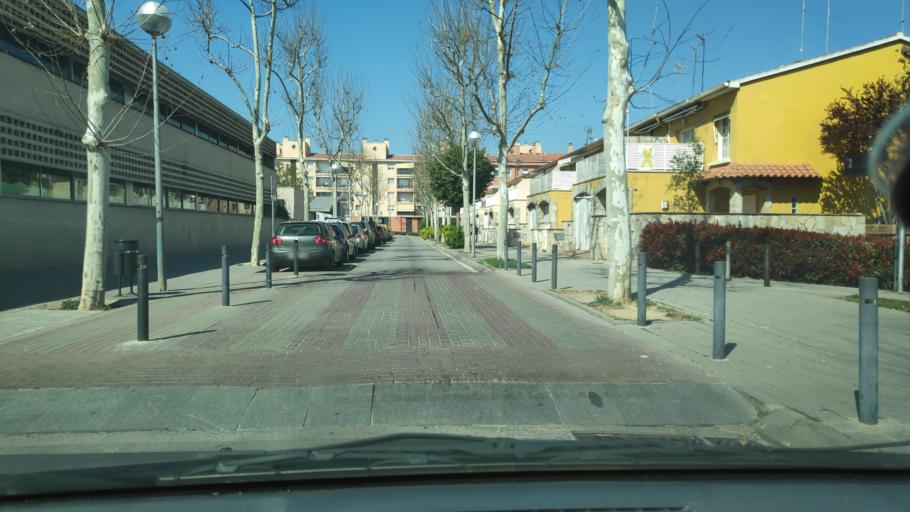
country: ES
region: Catalonia
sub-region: Provincia de Barcelona
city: Mollet del Valles
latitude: 41.5444
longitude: 2.2039
